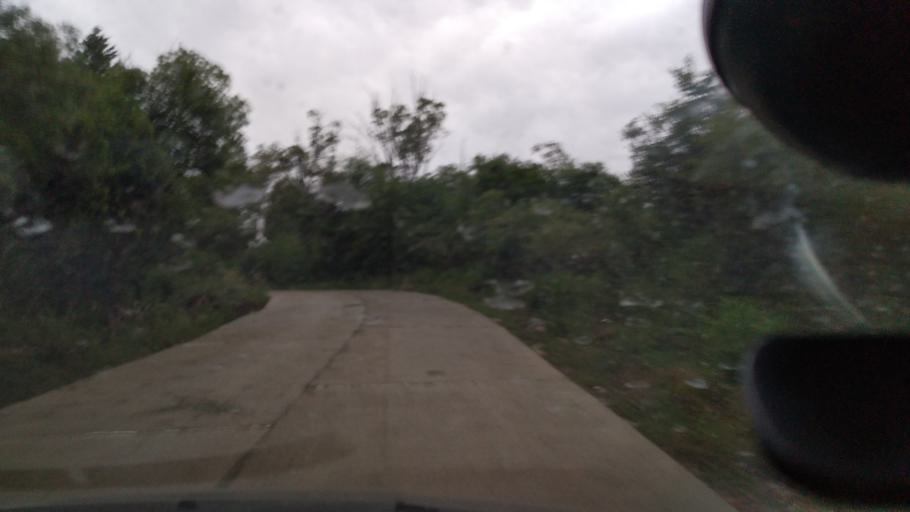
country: AR
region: Cordoba
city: Villa Las Rosas
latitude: -31.8789
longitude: -65.0245
